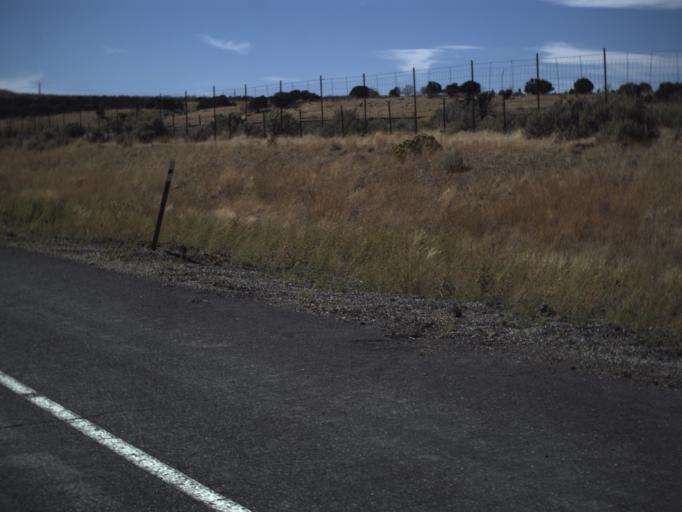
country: US
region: Utah
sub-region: Beaver County
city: Beaver
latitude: 38.5795
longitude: -112.5995
